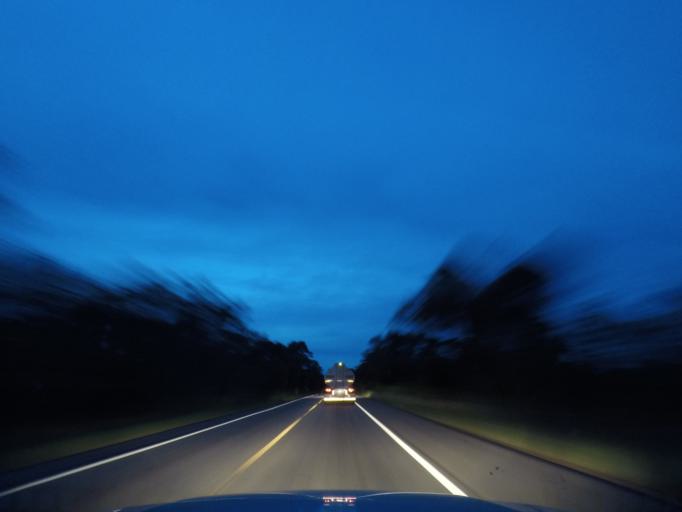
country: BR
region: Bahia
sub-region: Andarai
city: Vera Cruz
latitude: -12.4884
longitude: -41.3413
